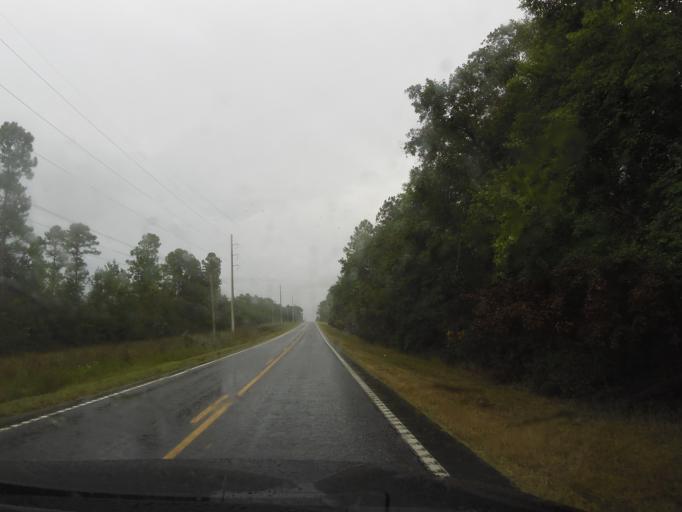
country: US
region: Florida
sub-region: Baker County
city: Macclenny
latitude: 30.3888
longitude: -82.1275
